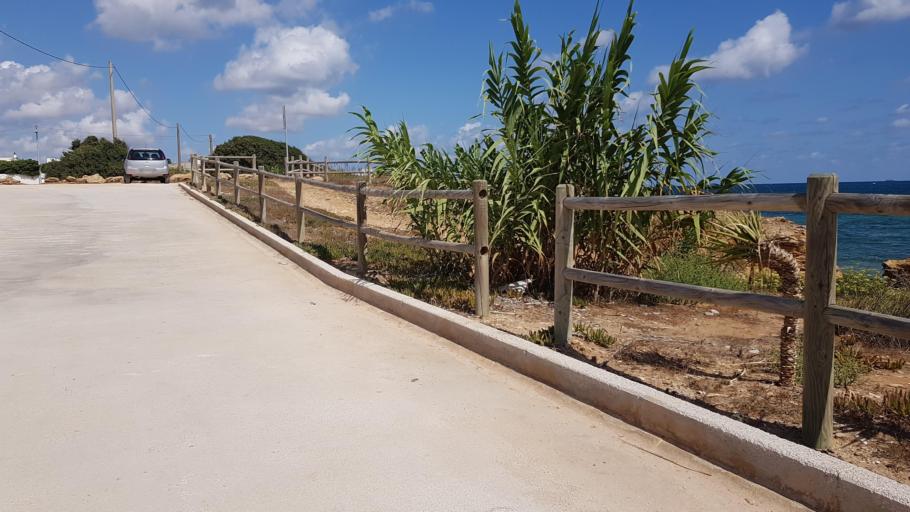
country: IT
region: Apulia
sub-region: Provincia di Brindisi
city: Torchiarolo
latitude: 40.5263
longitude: 18.0797
